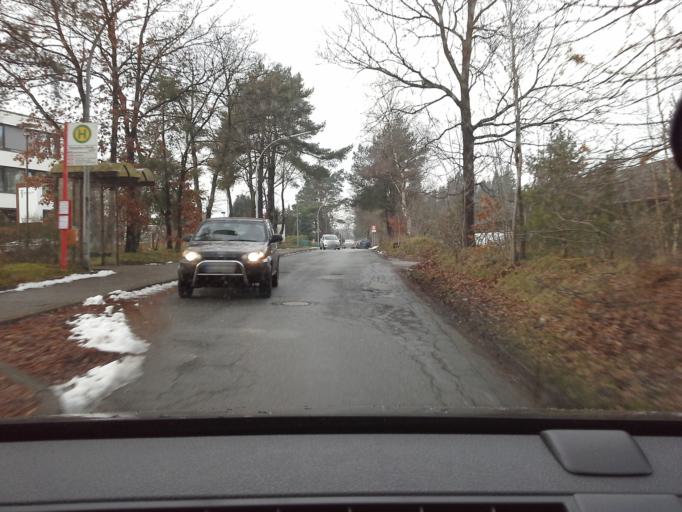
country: DE
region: Schleswig-Holstein
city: Henstedt-Ulzburg
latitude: 53.7494
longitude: 10.0089
